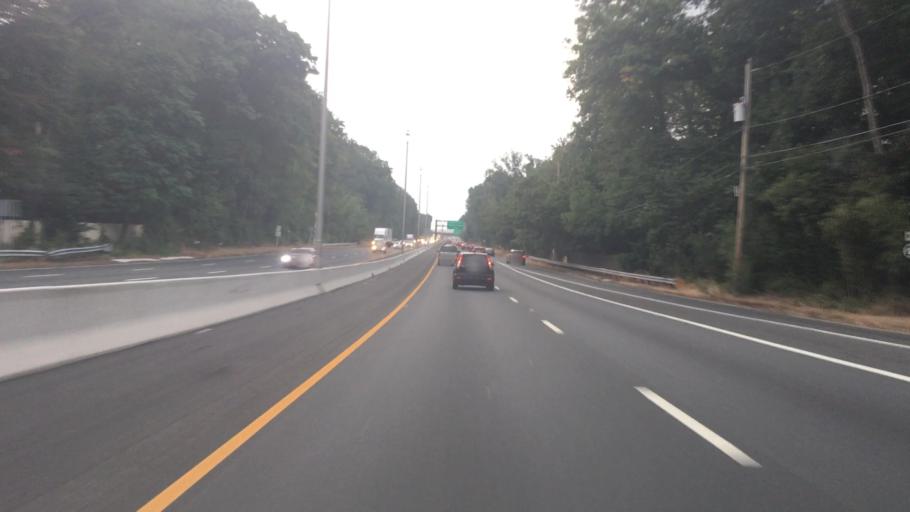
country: US
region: New Jersey
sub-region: Bergen County
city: Franklin Lakes
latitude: 41.0084
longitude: -74.1948
